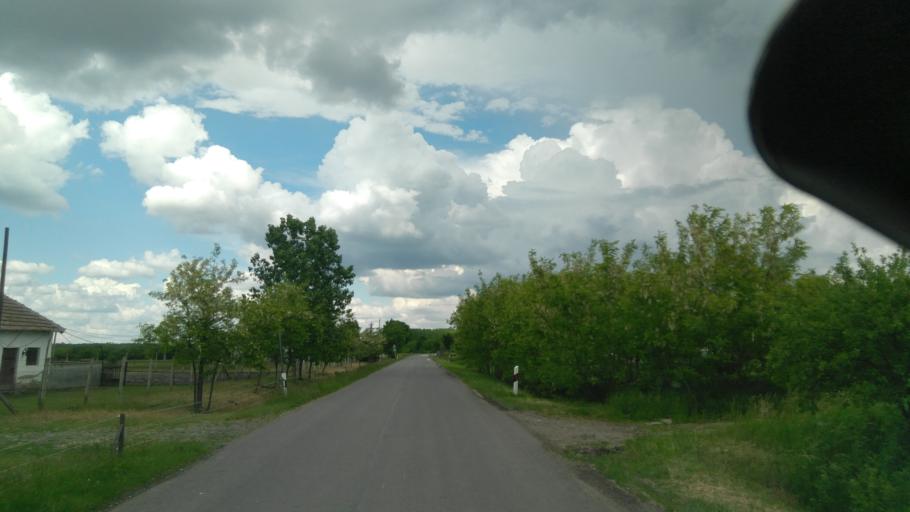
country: HU
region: Bekes
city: Bucsa
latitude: 47.1531
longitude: 21.0662
